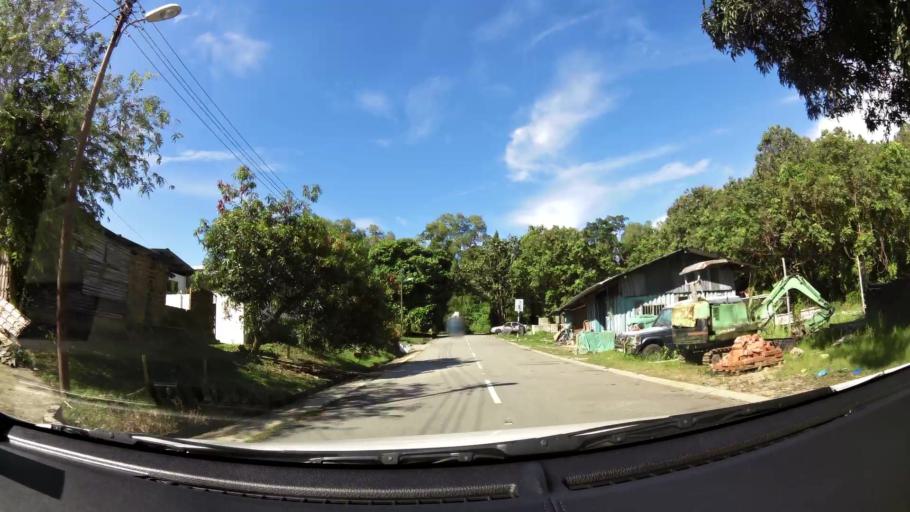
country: BN
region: Brunei and Muara
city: Bandar Seri Begawan
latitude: 4.9675
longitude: 114.9285
